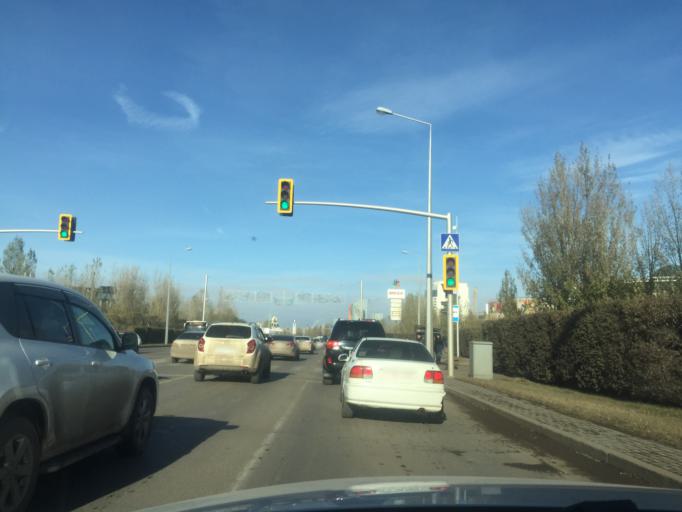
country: KZ
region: Astana Qalasy
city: Astana
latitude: 51.1434
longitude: 71.4112
